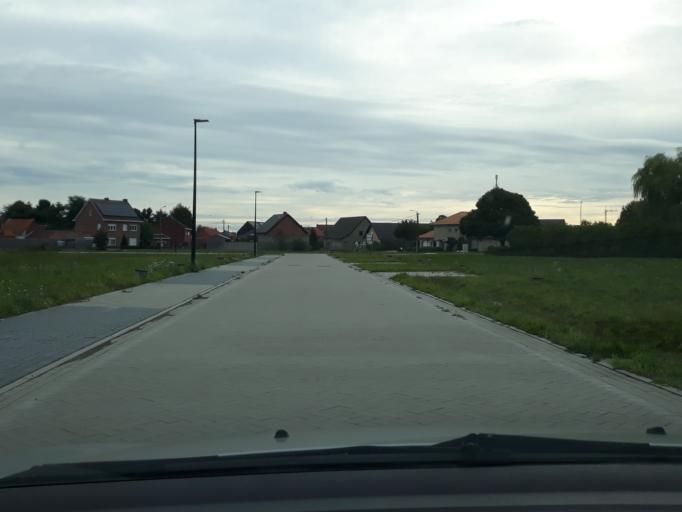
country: BE
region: Flanders
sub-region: Provincie Antwerpen
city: Ravels
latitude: 51.3701
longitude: 4.9860
